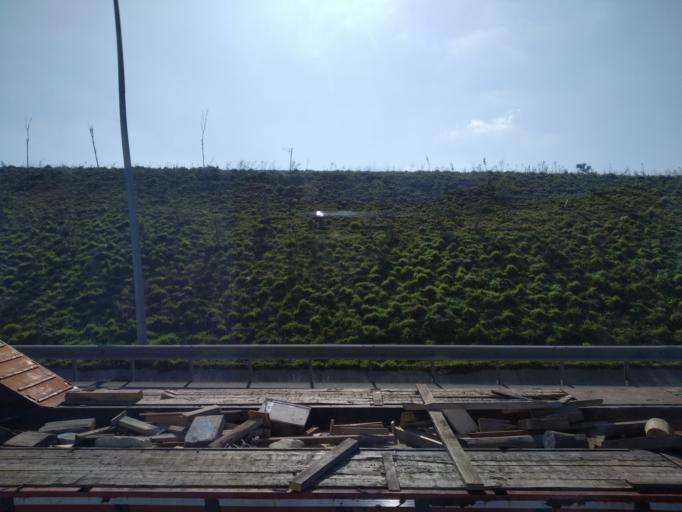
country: TR
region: Istanbul
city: Kemerburgaz
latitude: 41.2298
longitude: 28.8539
